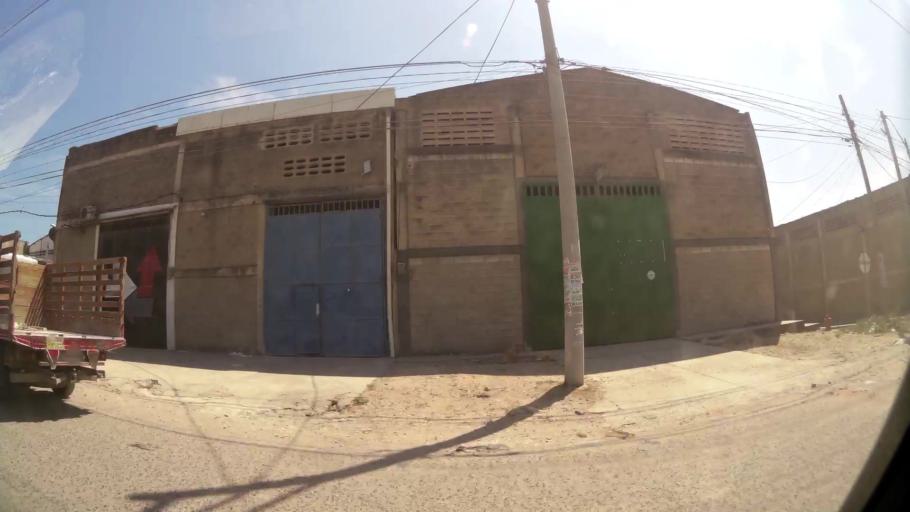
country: CO
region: Atlantico
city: Barranquilla
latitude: 10.9820
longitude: -74.8388
